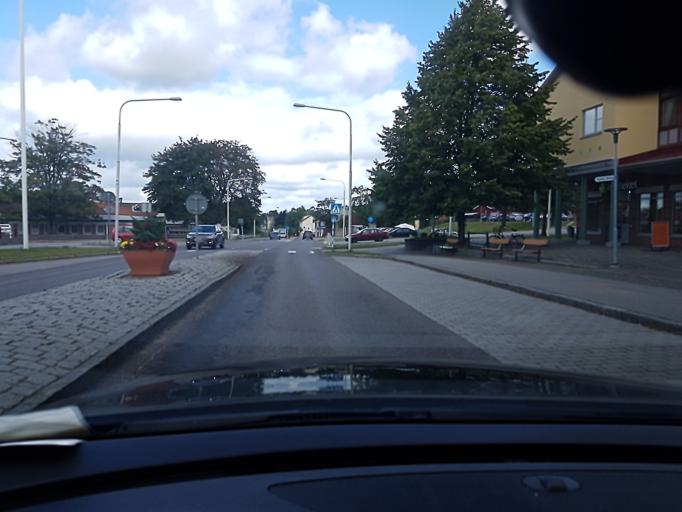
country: SE
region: Kronoberg
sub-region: Lessebo Kommun
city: Lessebo
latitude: 56.7513
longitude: 15.2699
